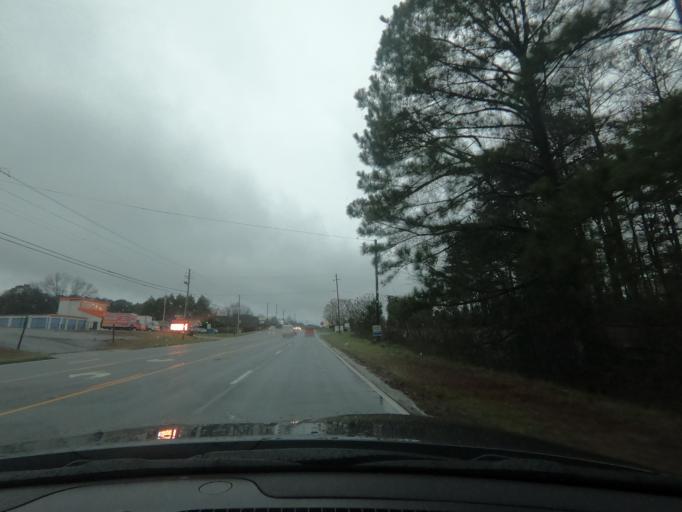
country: US
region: Georgia
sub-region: Cherokee County
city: Woodstock
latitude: 34.0713
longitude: -84.5218
